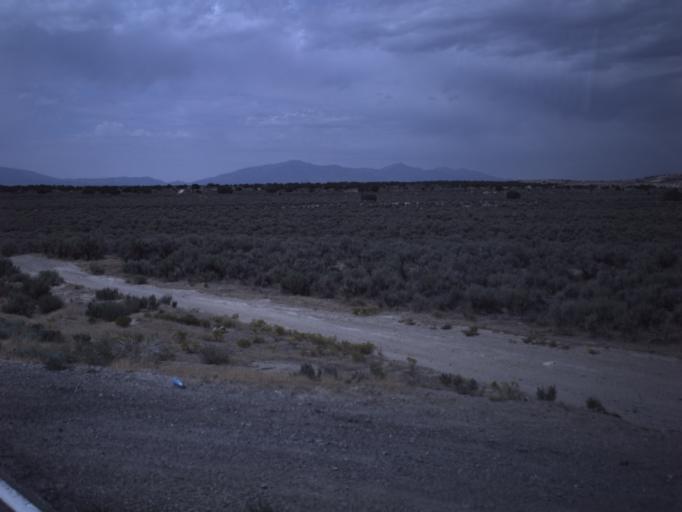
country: US
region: Utah
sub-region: Utah County
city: Eagle Mountain
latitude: 40.2311
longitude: -112.1813
